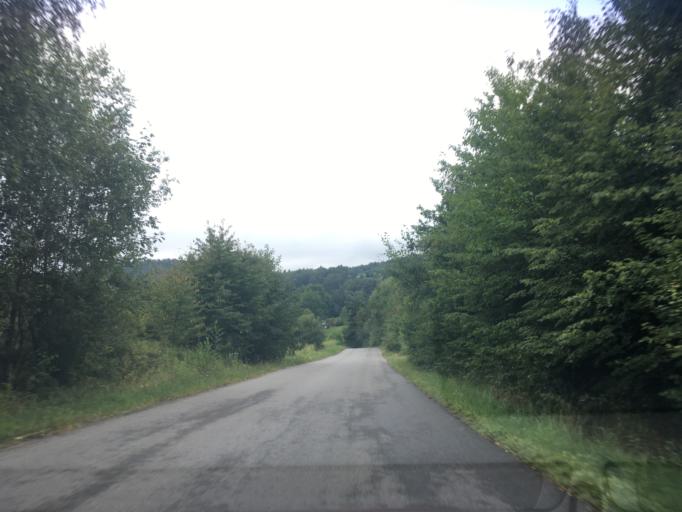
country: PL
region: Lesser Poland Voivodeship
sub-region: Powiat myslenicki
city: Brzaczowice
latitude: 49.8552
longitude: 20.0208
